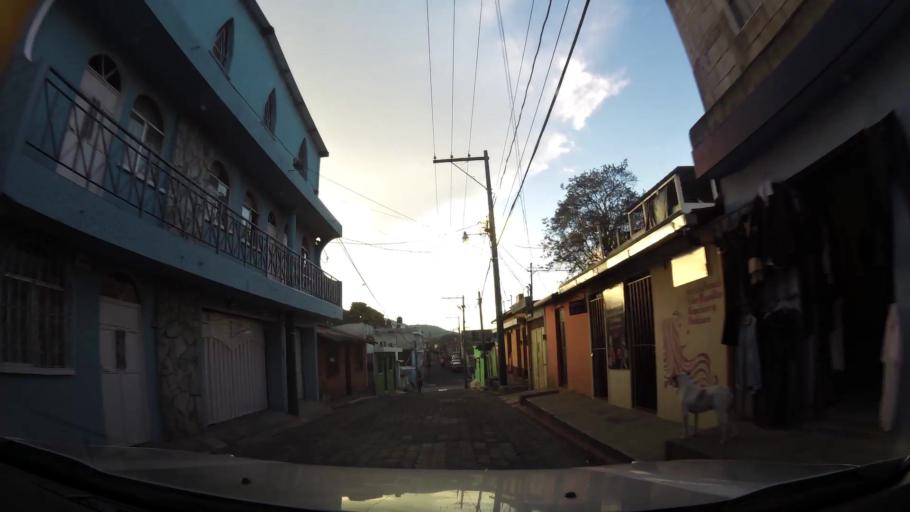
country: GT
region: Sacatepequez
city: San Lucas Sacatepequez
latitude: 14.6113
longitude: -90.6552
